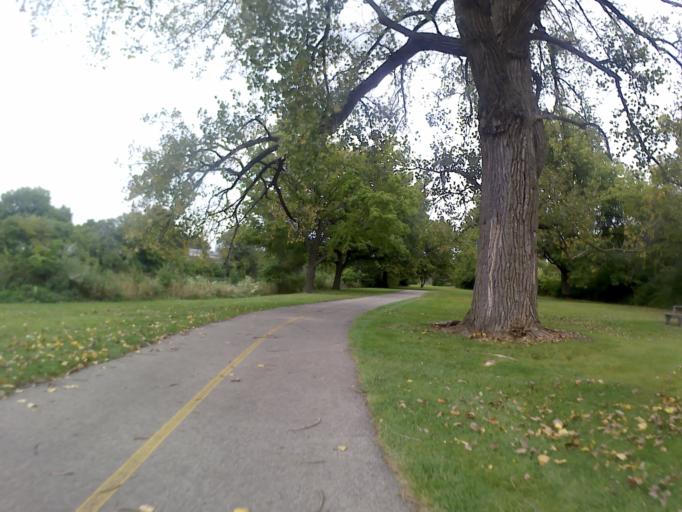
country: US
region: Illinois
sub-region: Kane County
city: Montgomery
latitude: 41.7399
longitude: -88.3295
